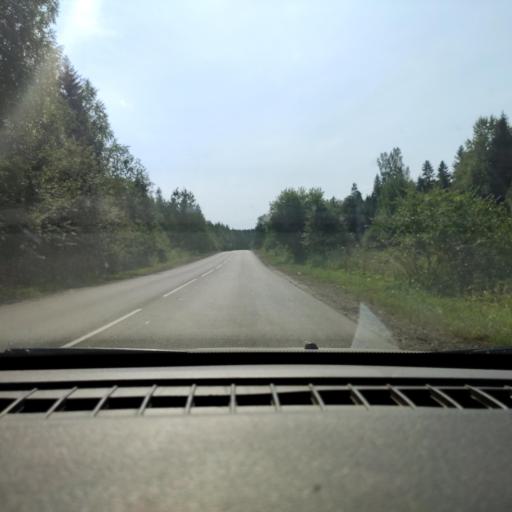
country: RU
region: Perm
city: Novyye Lyady
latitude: 58.1244
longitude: 56.4670
